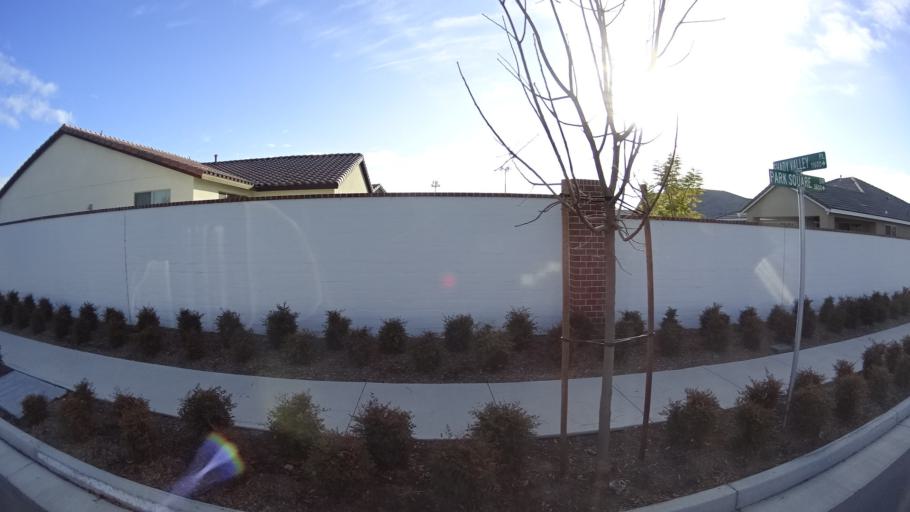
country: US
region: California
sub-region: Kern County
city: Rosedale
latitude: 35.3208
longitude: -119.1313
